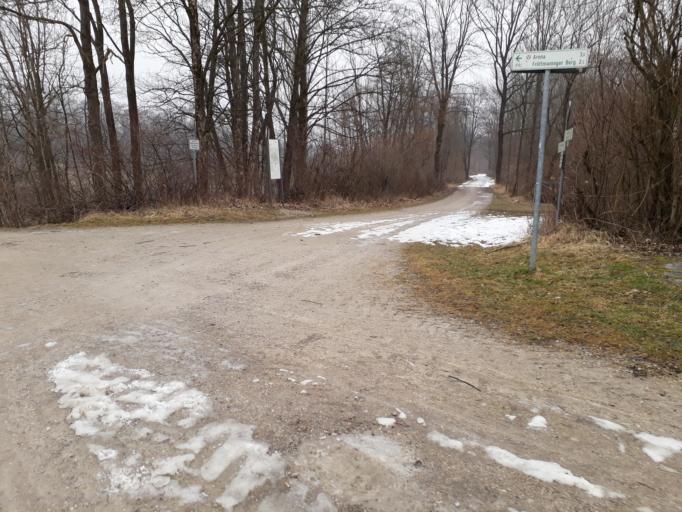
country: DE
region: Bavaria
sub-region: Upper Bavaria
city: Unterfoehring
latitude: 48.2060
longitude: 11.6439
